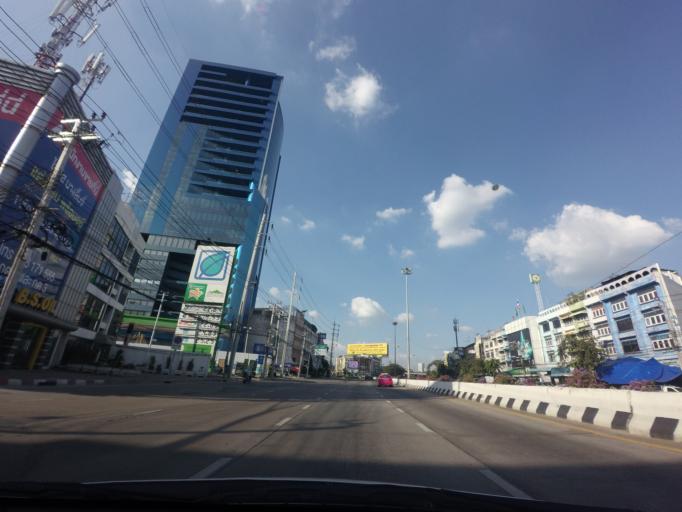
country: TH
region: Bangkok
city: Yan Nawa
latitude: 13.7006
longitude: 100.5455
